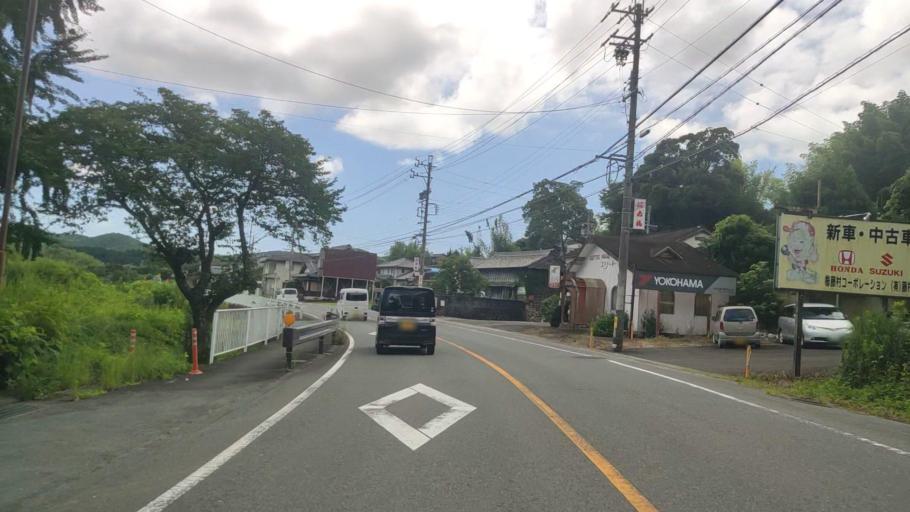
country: JP
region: Mie
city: Toba
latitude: 34.4494
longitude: 136.8406
